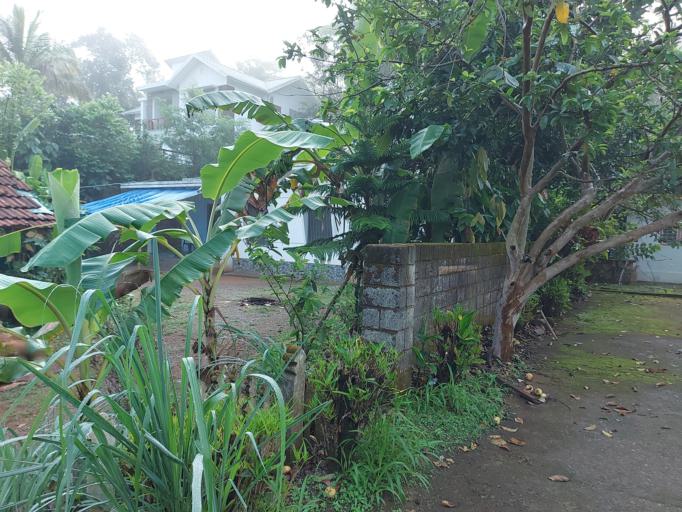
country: IN
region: Kerala
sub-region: Wayanad
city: Kalpetta
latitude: 11.6811
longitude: 75.9542
